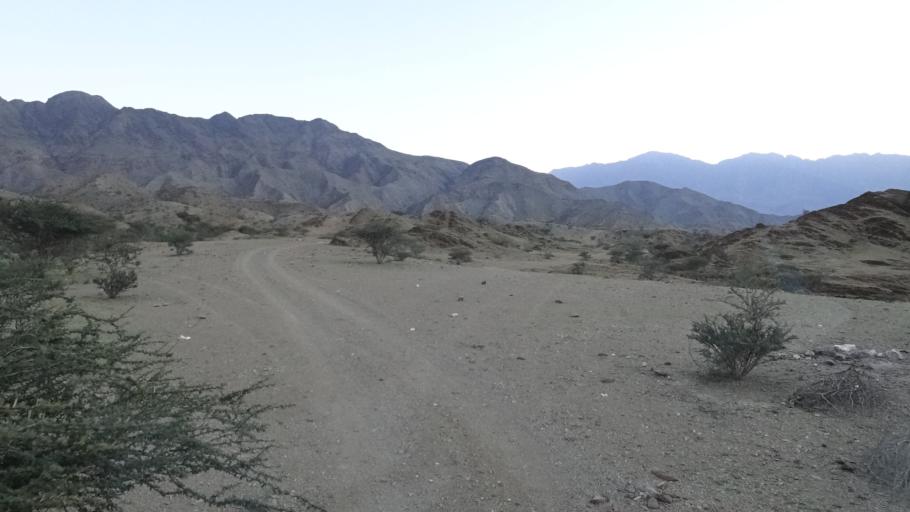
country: OM
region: Al Batinah
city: Rustaq
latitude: 23.2734
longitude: 57.3608
